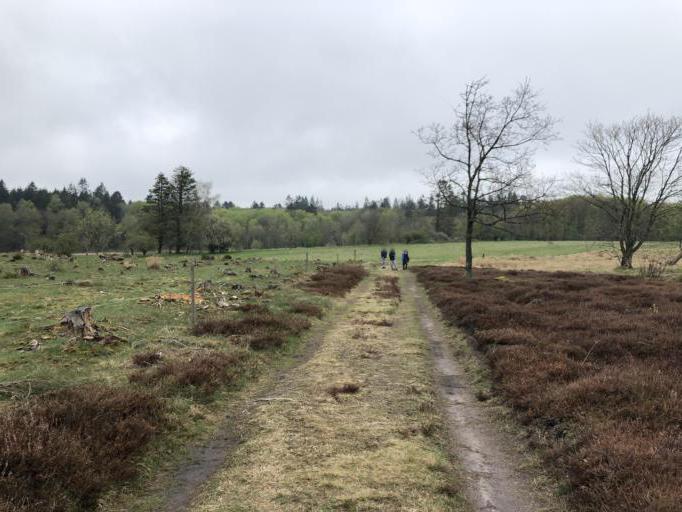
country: DK
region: Central Jutland
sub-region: Lemvig Kommune
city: Lemvig
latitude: 56.4824
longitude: 8.3609
